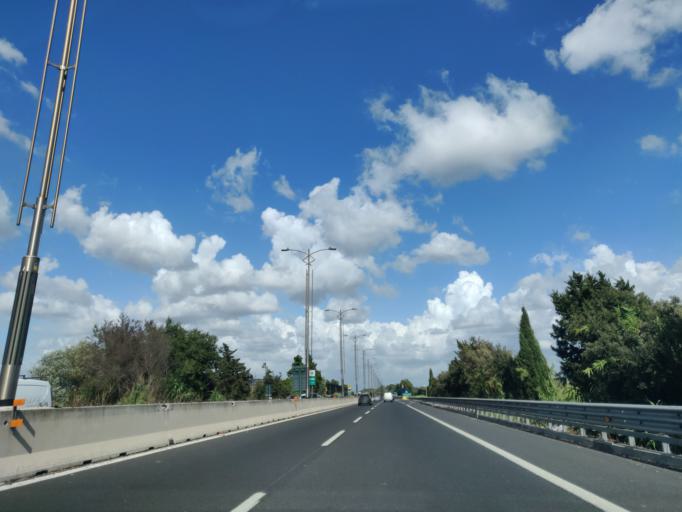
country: IT
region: Latium
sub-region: Citta metropolitana di Roma Capitale
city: Vitinia
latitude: 41.8190
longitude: 12.4003
